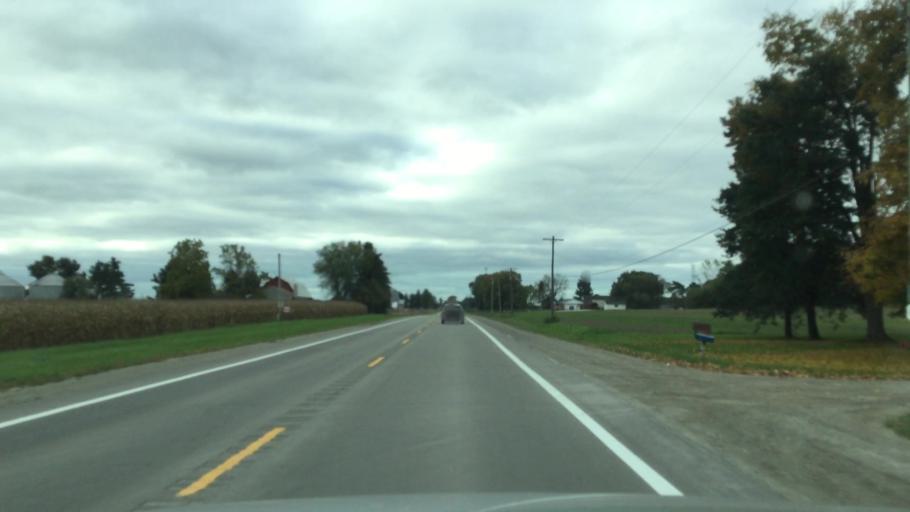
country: US
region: Michigan
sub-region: Macomb County
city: Memphis
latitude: 42.8726
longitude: -82.7676
